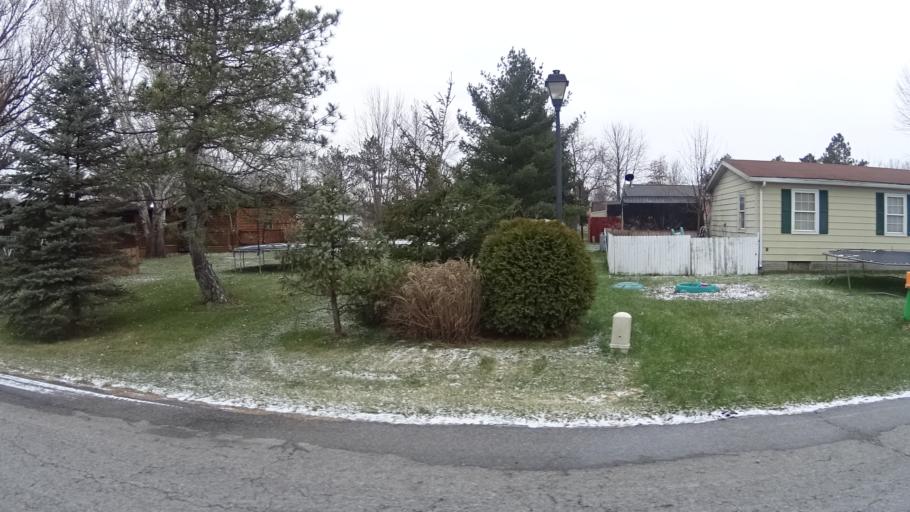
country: US
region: Ohio
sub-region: Lorain County
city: Lagrange
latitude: 41.2071
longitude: -82.1517
